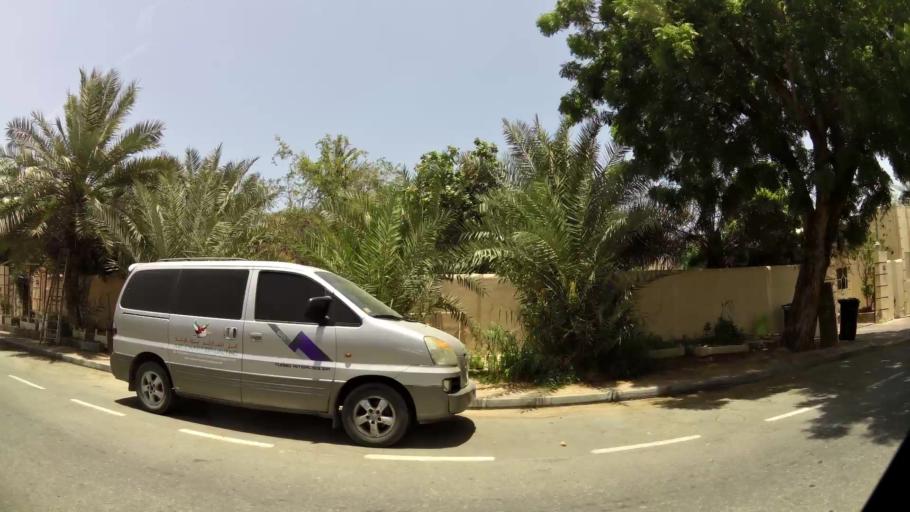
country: AE
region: Dubai
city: Dubai
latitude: 25.1751
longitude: 55.2222
